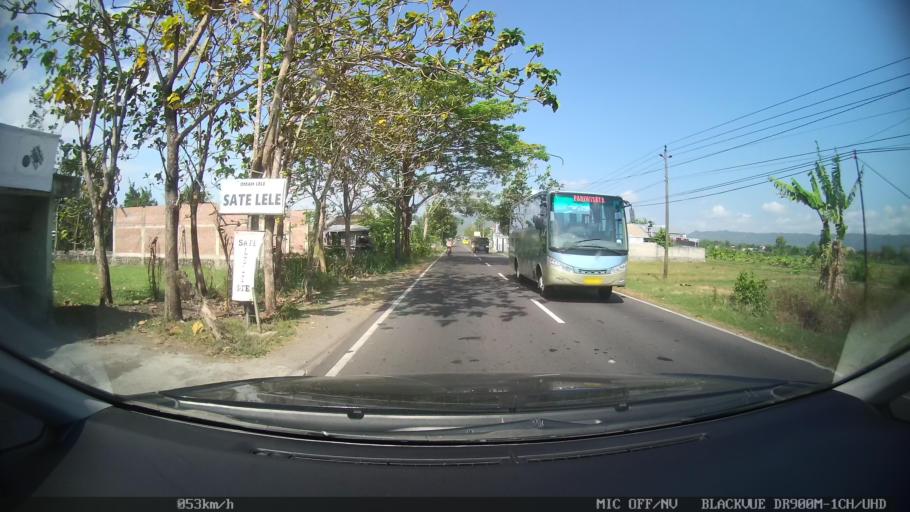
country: ID
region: Daerah Istimewa Yogyakarta
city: Sewon
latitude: -7.9110
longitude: 110.3585
